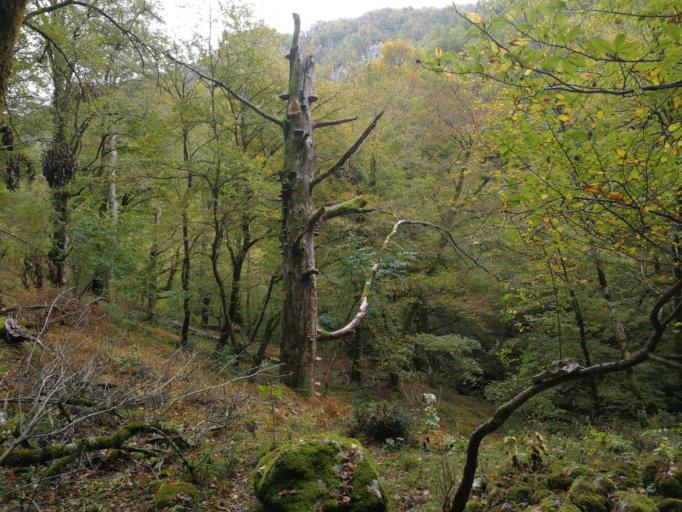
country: GE
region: Abkhazia
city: Gagra
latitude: 43.3301
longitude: 40.2689
